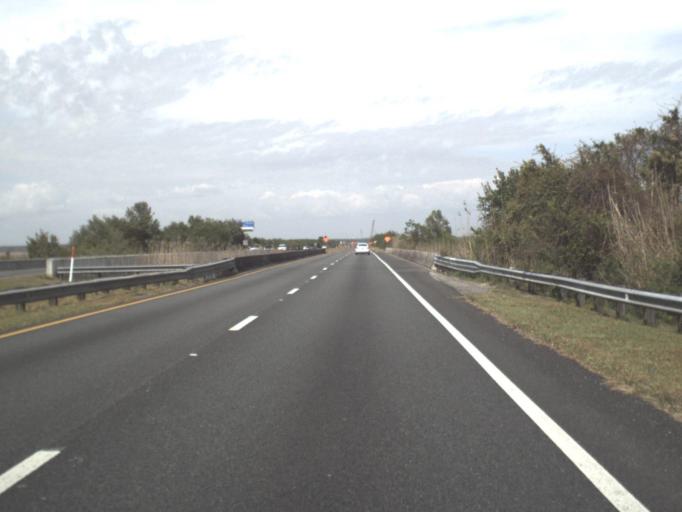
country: US
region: Florida
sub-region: Escambia County
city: Ferry Pass
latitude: 30.5544
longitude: -87.1929
